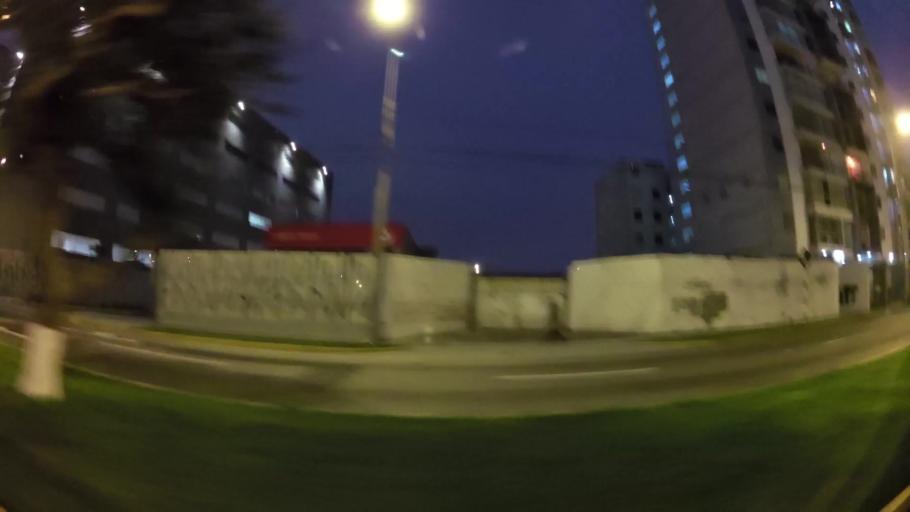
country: PE
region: Callao
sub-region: Callao
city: Callao
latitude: -12.0761
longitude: -77.0928
